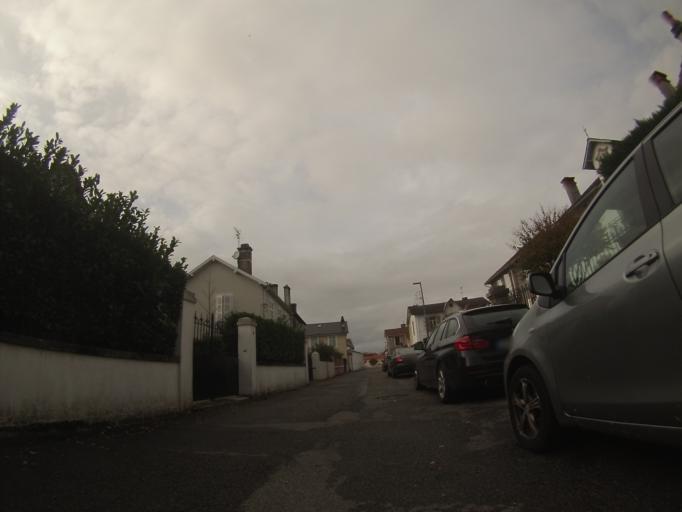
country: FR
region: Aquitaine
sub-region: Departement des Pyrenees-Atlantiques
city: Jurancon
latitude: 43.2885
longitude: -0.3862
